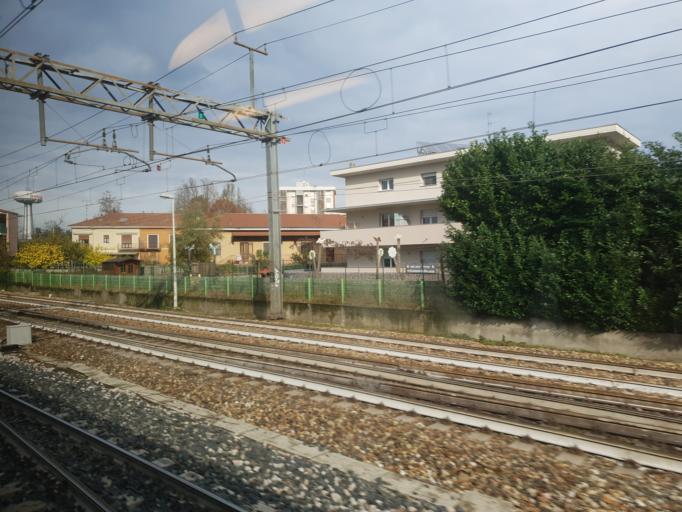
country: IT
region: Lombardy
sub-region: Provincia di Varese
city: Saronno
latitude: 45.6192
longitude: 9.0386
